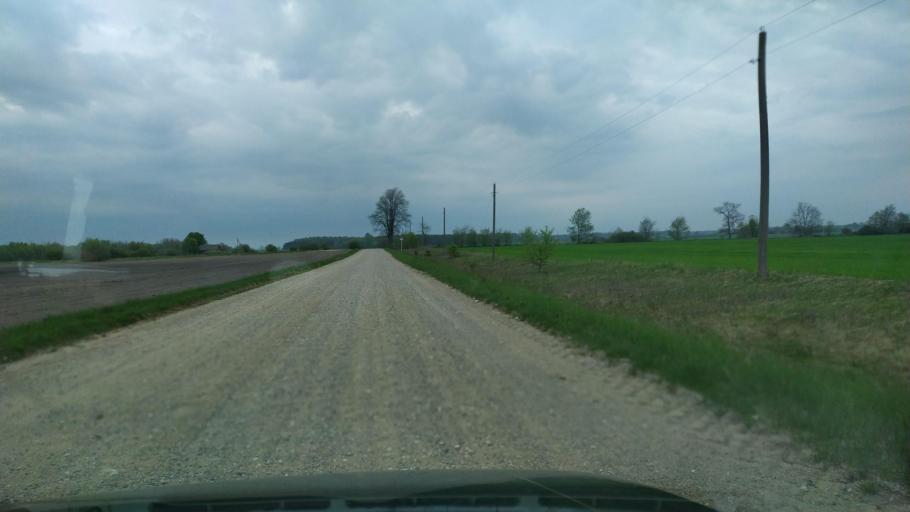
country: BY
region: Brest
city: Zhabinka
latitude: 52.1331
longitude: 24.0923
